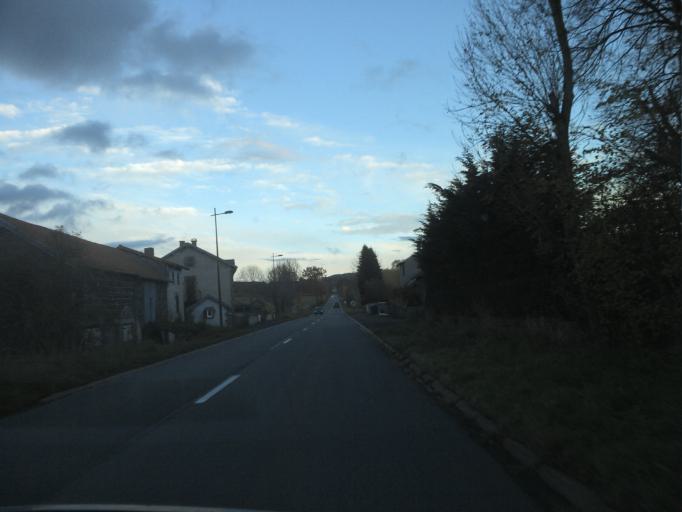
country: FR
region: Auvergne
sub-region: Departement du Puy-de-Dome
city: Saint-Ours
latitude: 45.8288
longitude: 2.8991
